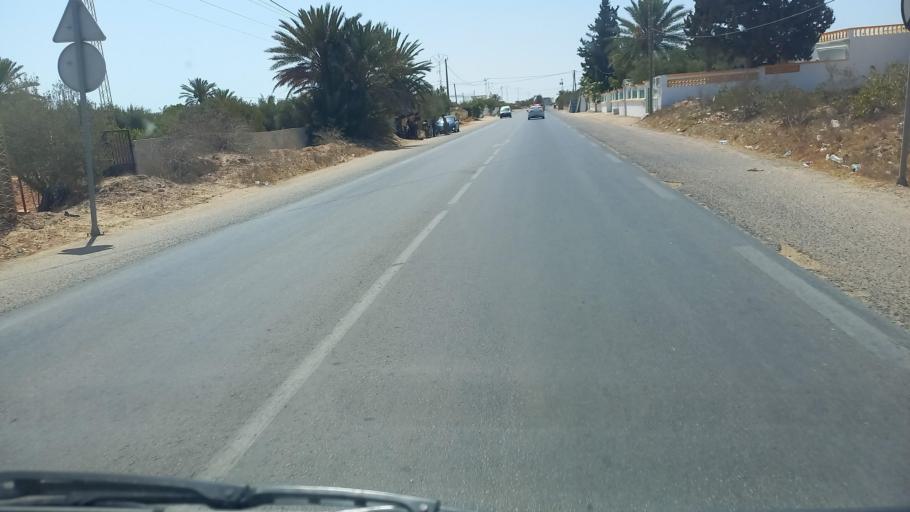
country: TN
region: Madanin
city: Houmt Souk
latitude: 33.7928
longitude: 10.8872
